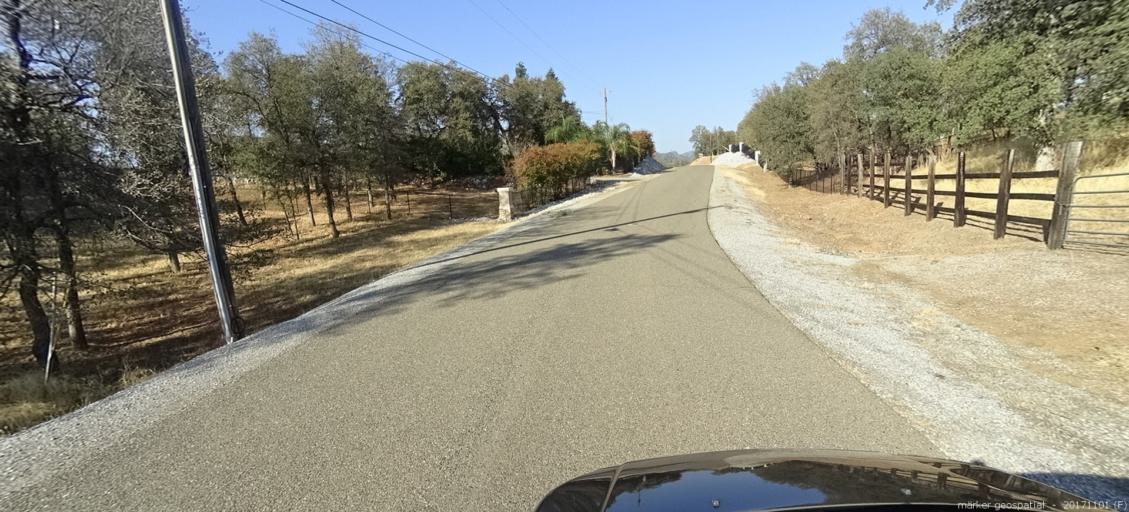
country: US
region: California
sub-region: Shasta County
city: Bella Vista
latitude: 40.6755
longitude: -122.2912
